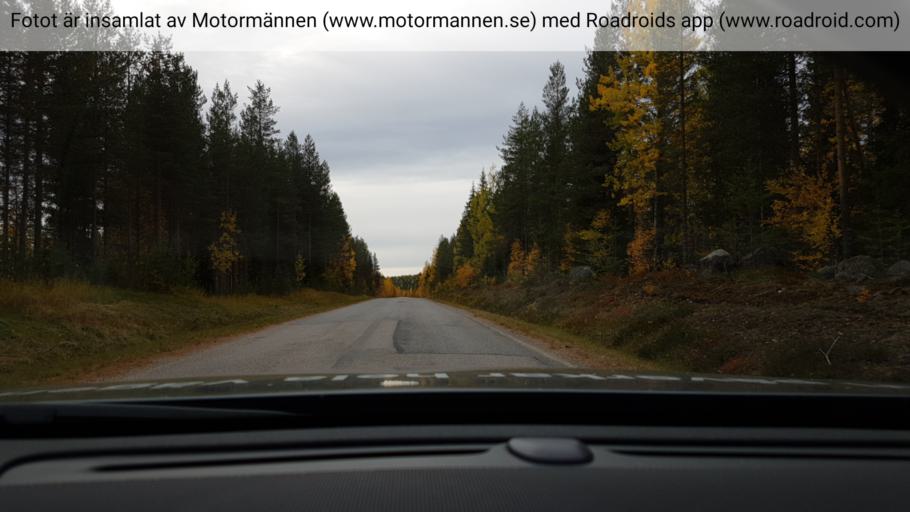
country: SE
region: Norrbotten
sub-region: Overkalix Kommun
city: OEverkalix
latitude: 66.2545
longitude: 23.0173
